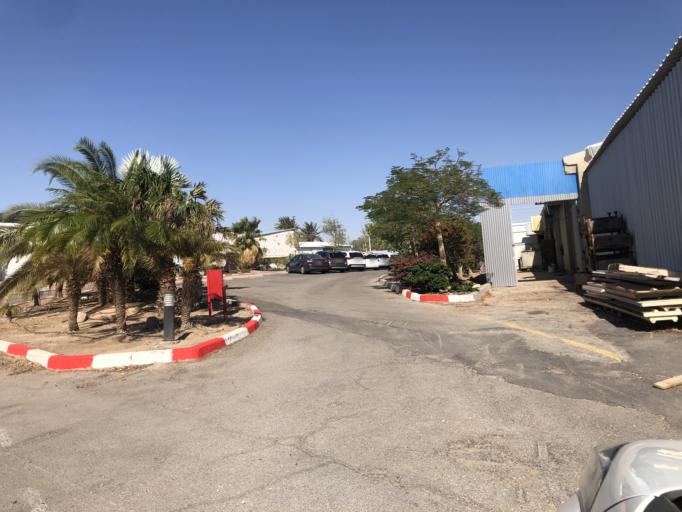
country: IL
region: Southern District
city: Eilat
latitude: 29.5805
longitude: 34.9640
